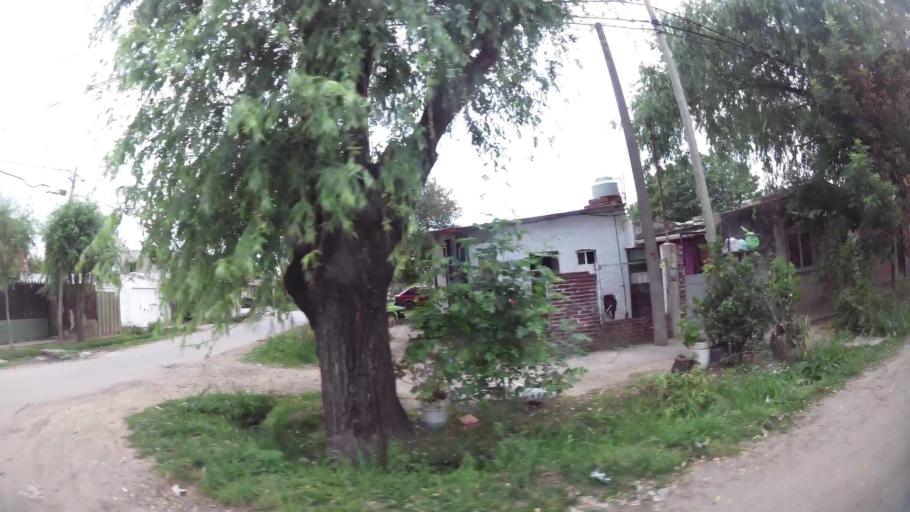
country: AR
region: Buenos Aires
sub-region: Partido de Zarate
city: Zarate
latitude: -34.1160
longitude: -59.0331
